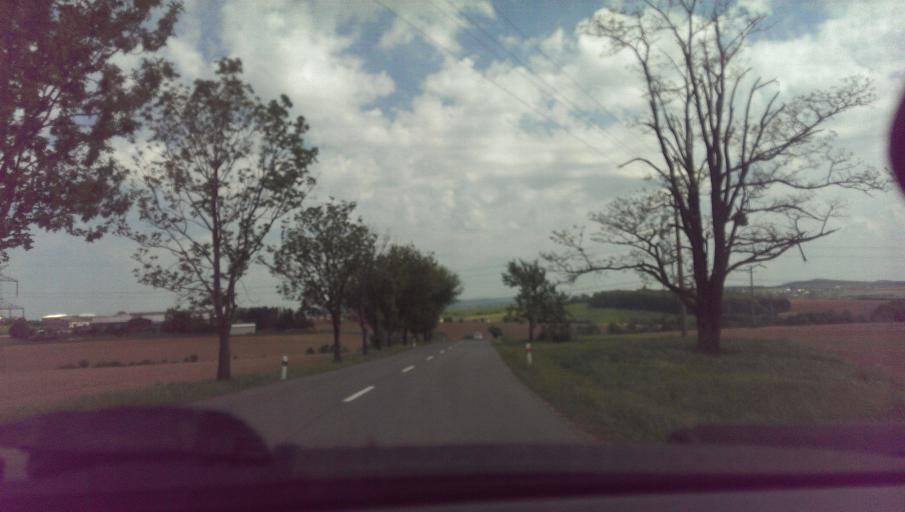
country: CZ
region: Zlin
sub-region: Okres Zlin
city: Otrokovice
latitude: 49.2444
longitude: 17.5396
